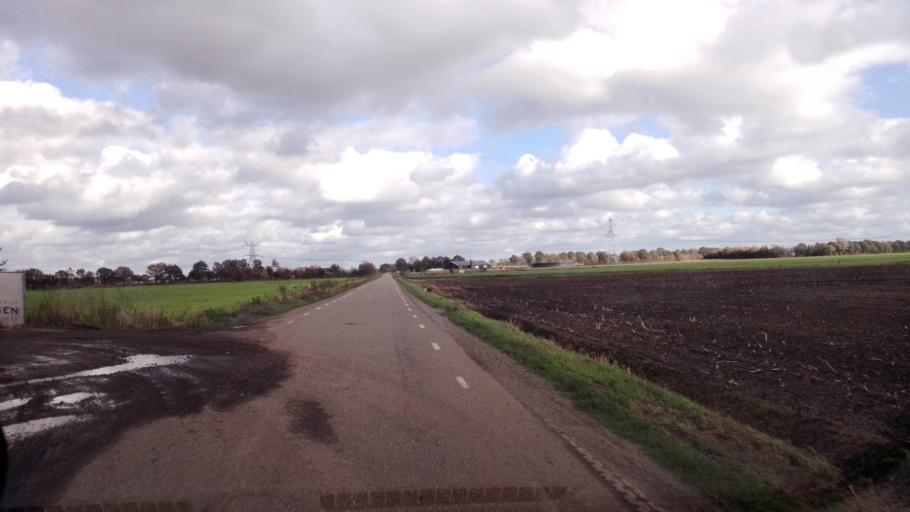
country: NL
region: Limburg
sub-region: Gemeente Venray
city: Venray
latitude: 51.4825
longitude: 5.9189
